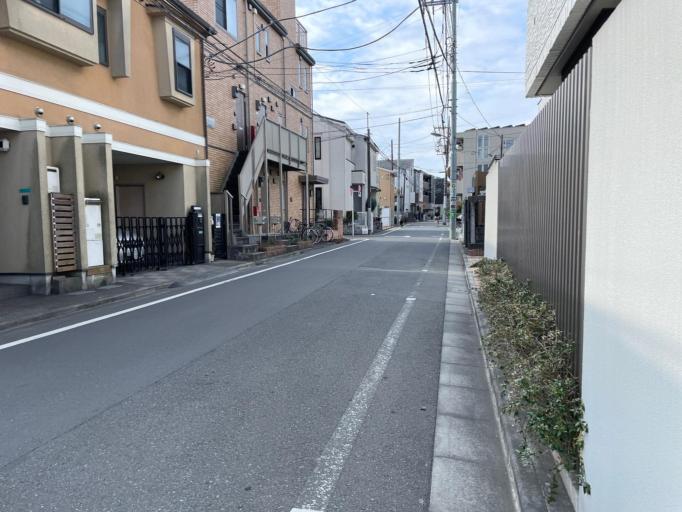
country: JP
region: Tokyo
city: Tokyo
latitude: 35.7422
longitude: 139.6773
